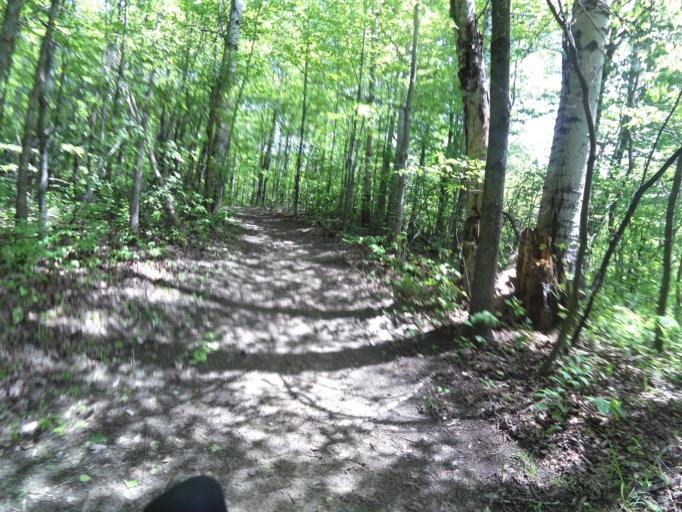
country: CA
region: Ontario
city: Ottawa
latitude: 45.3922
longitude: -75.5197
